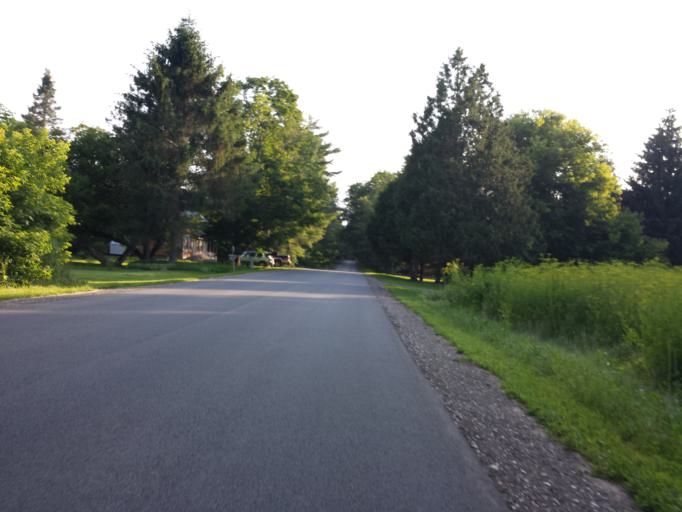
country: US
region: New York
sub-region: St. Lawrence County
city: Norwood
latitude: 44.7158
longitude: -74.9710
